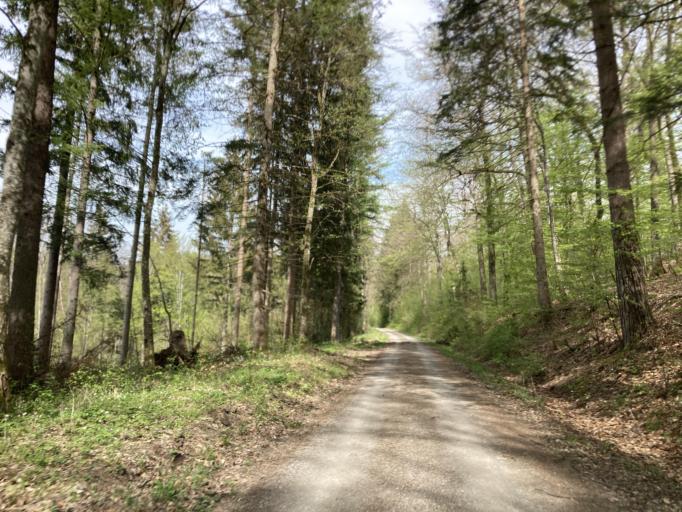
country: DE
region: Baden-Wuerttemberg
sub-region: Tuebingen Region
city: Rottenburg
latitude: 48.4600
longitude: 8.9909
